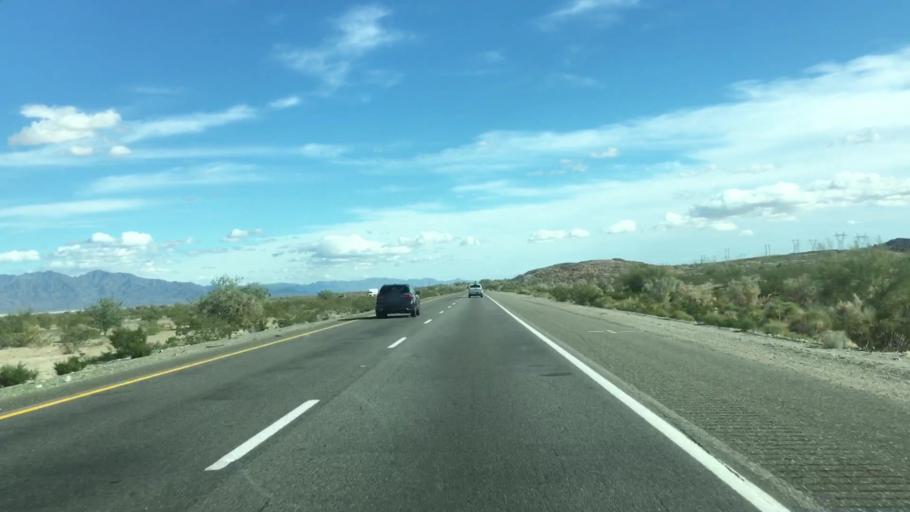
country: US
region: California
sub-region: Imperial County
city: Niland
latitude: 33.7079
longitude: -115.3591
